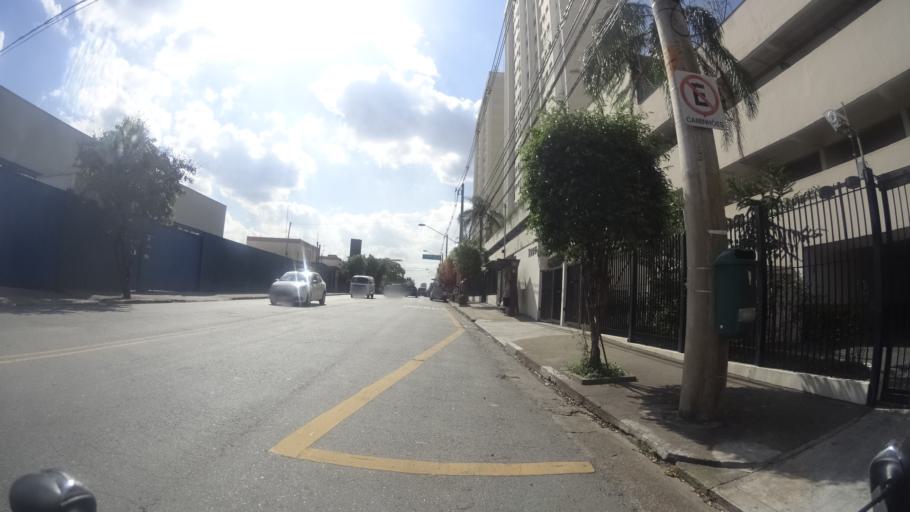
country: BR
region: Sao Paulo
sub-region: Sao Paulo
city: Sao Paulo
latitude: -23.5786
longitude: -46.5925
